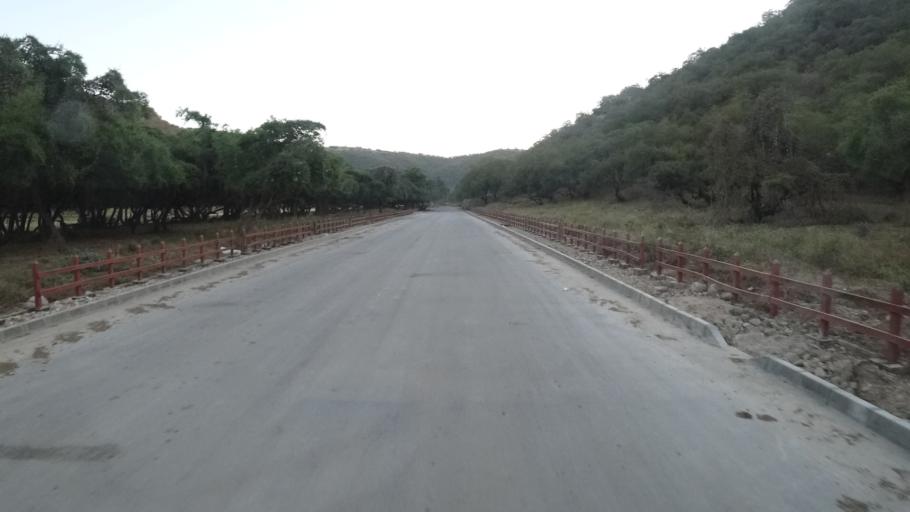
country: OM
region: Zufar
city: Salalah
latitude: 17.0969
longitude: 54.4496
